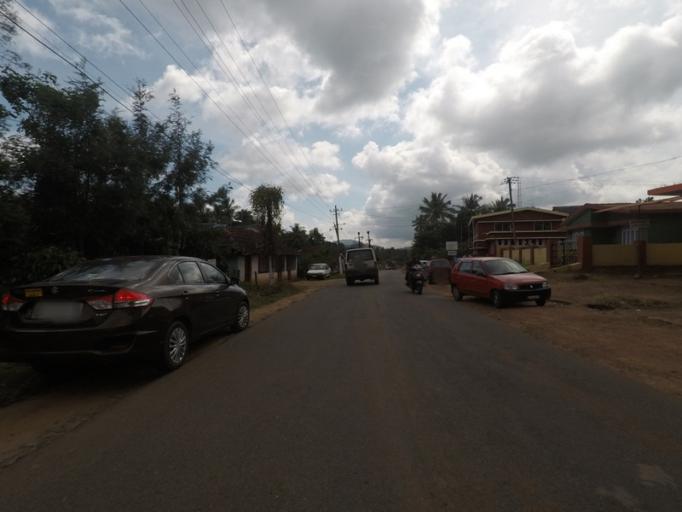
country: IN
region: Karnataka
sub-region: Kodagu
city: Virarajendrapet
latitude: 12.2386
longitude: 75.8560
